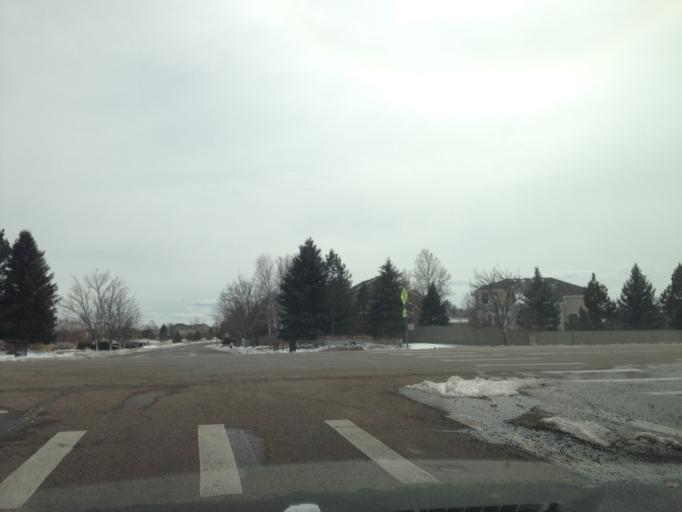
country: US
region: Colorado
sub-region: Boulder County
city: Lafayette
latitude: 39.9727
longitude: -105.0951
